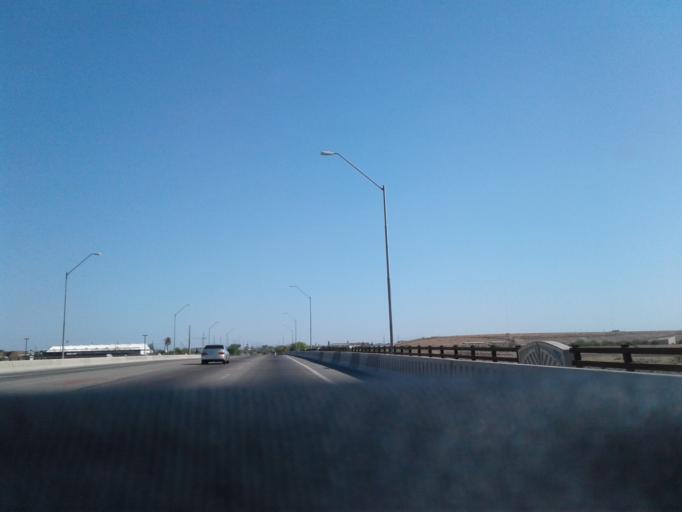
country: US
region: Arizona
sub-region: Maricopa County
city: Laveen
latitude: 33.4102
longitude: -112.1338
